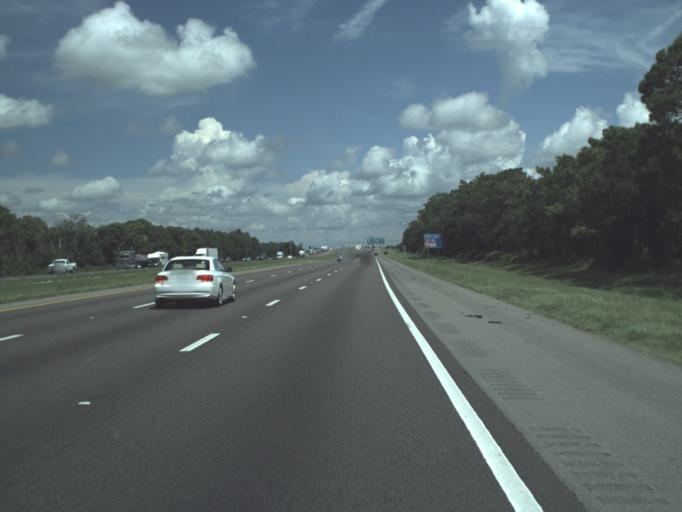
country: US
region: Florida
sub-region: Sarasota County
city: Desoto Lakes
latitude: 27.4311
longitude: -82.4593
